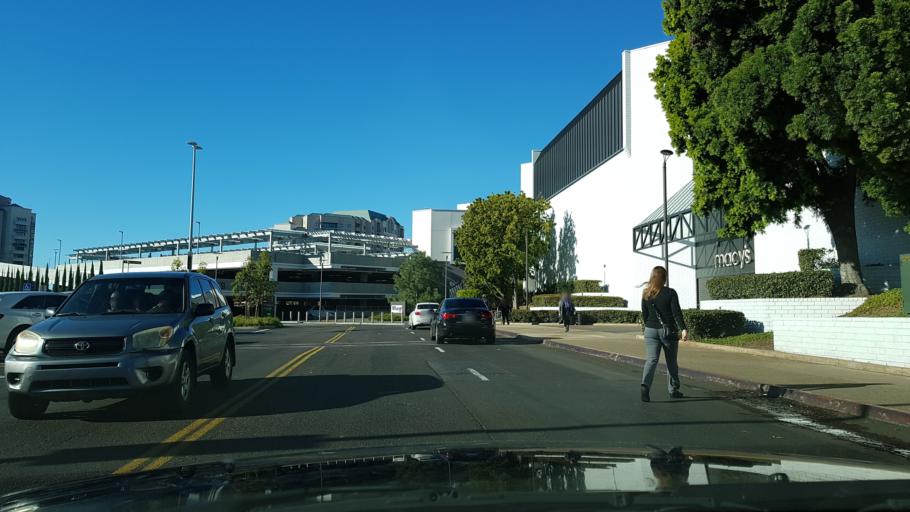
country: US
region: California
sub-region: San Diego County
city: La Jolla
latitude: 32.8686
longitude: -117.2124
